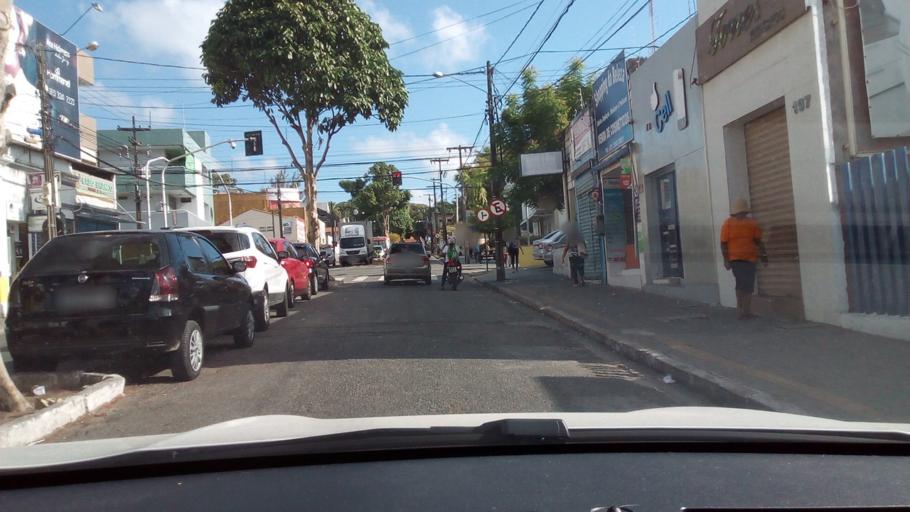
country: BR
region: Paraiba
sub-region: Joao Pessoa
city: Joao Pessoa
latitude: -7.1173
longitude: -34.8789
